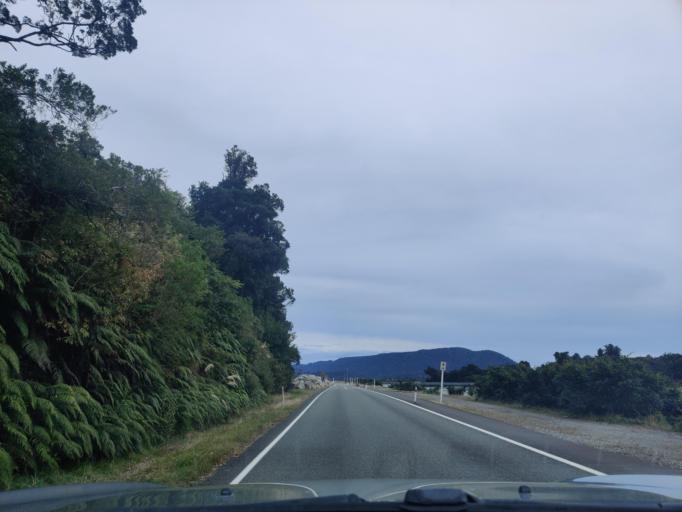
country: NZ
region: West Coast
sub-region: Westland District
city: Hokitika
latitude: -43.3971
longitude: 170.1815
